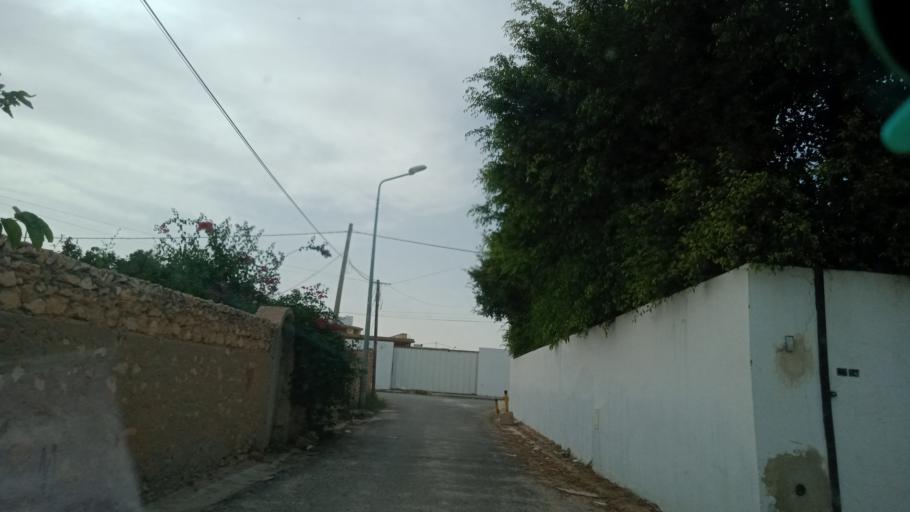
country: TN
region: Safaqis
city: Al Qarmadah
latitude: 34.8001
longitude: 10.7544
